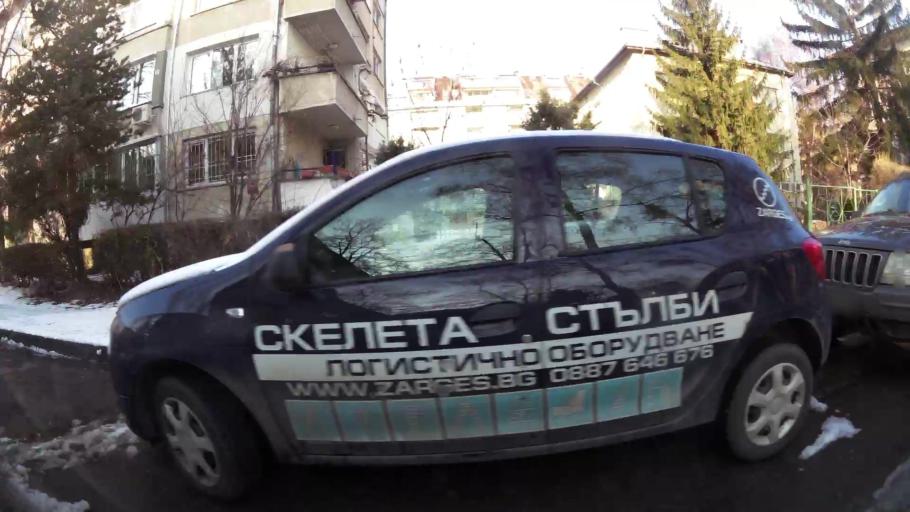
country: BG
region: Sofia-Capital
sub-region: Stolichna Obshtina
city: Sofia
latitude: 42.6777
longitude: 23.3629
